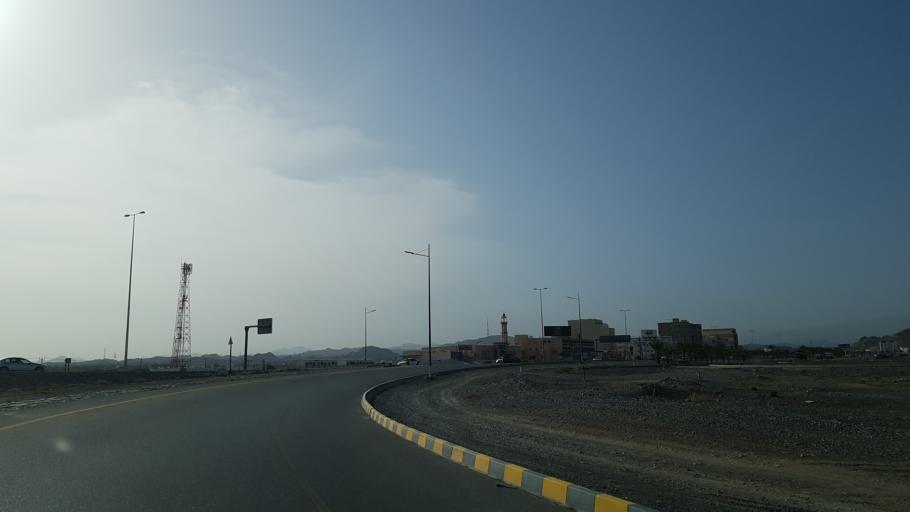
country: OM
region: Muhafazat ad Dakhiliyah
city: Nizwa
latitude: 22.8611
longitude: 57.5398
